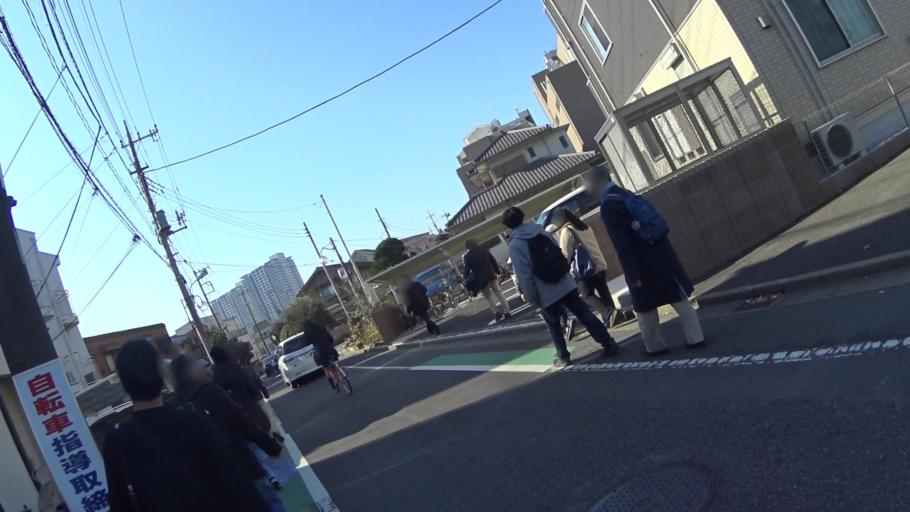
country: JP
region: Saitama
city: Saitama
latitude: 35.9076
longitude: 139.6364
